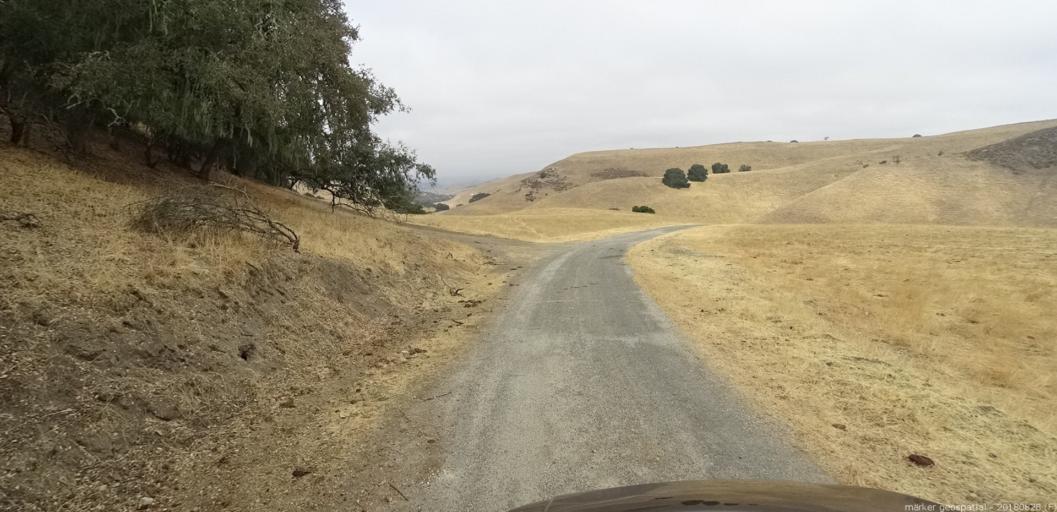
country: US
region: California
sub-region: San Luis Obispo County
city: San Miguel
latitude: 35.9372
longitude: -120.7356
